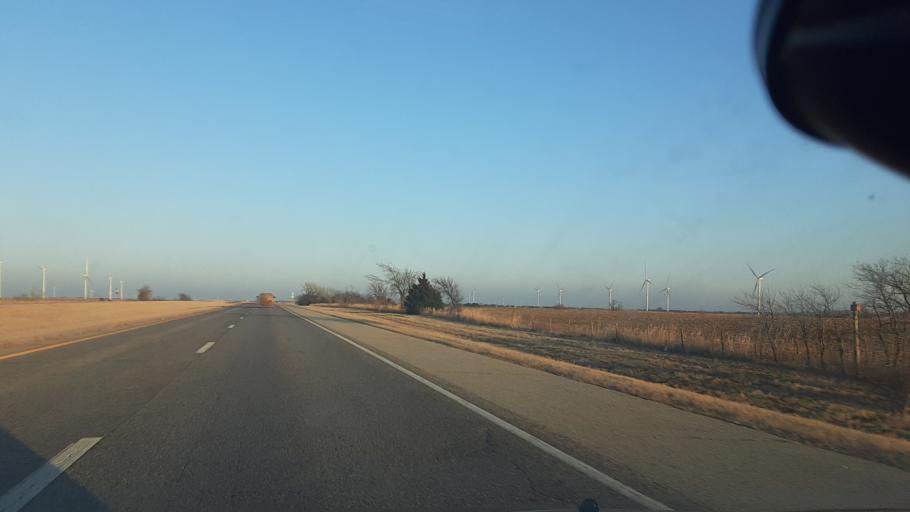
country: US
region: Oklahoma
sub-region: Noble County
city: Perry
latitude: 36.3975
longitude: -97.5210
